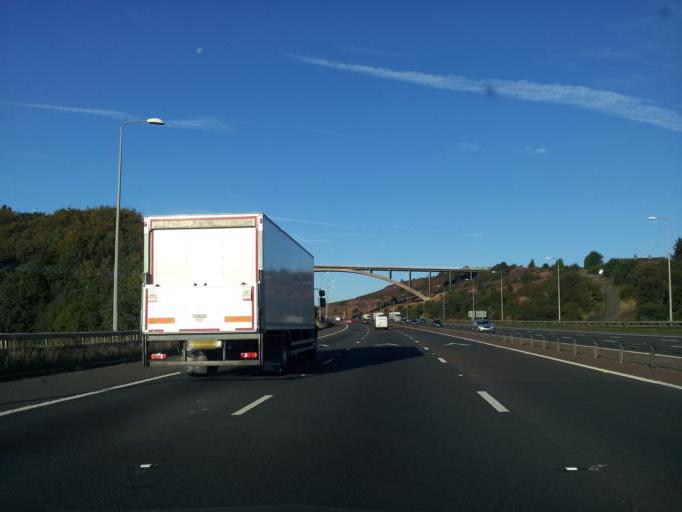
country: GB
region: England
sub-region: Calderdale
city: Ripponden
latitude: 53.6472
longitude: -1.9252
